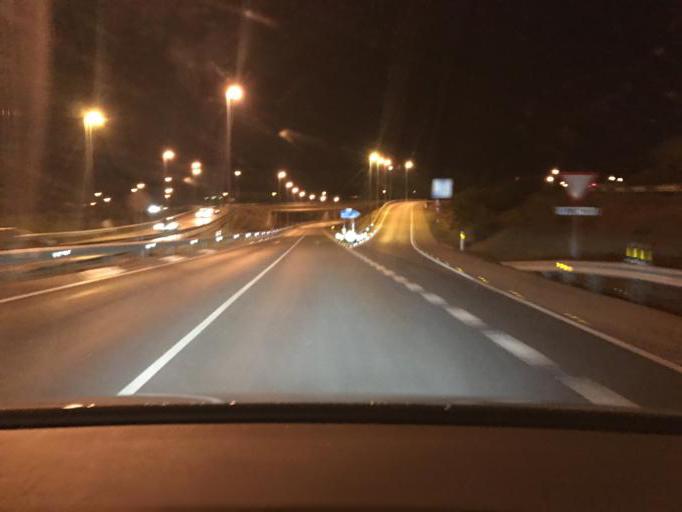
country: ES
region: Andalusia
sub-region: Provincia de Jaen
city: Jaen
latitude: 37.7818
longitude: -3.7594
